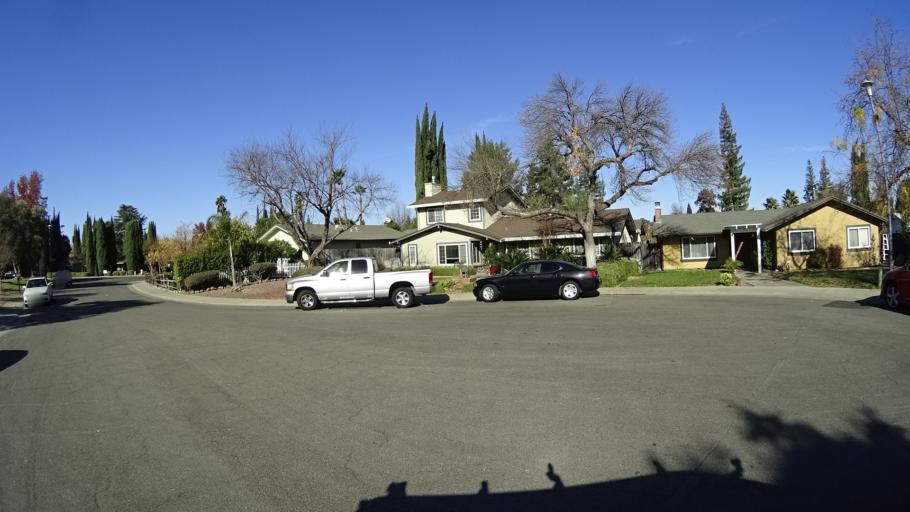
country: US
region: California
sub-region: Sacramento County
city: Antelope
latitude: 38.6806
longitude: -121.3110
